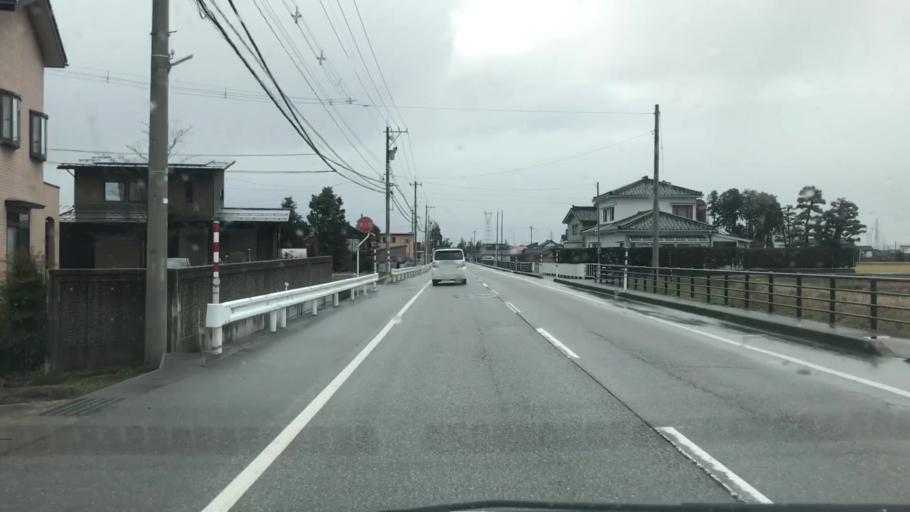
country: JP
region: Toyama
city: Kamiichi
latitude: 36.6763
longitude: 137.2903
